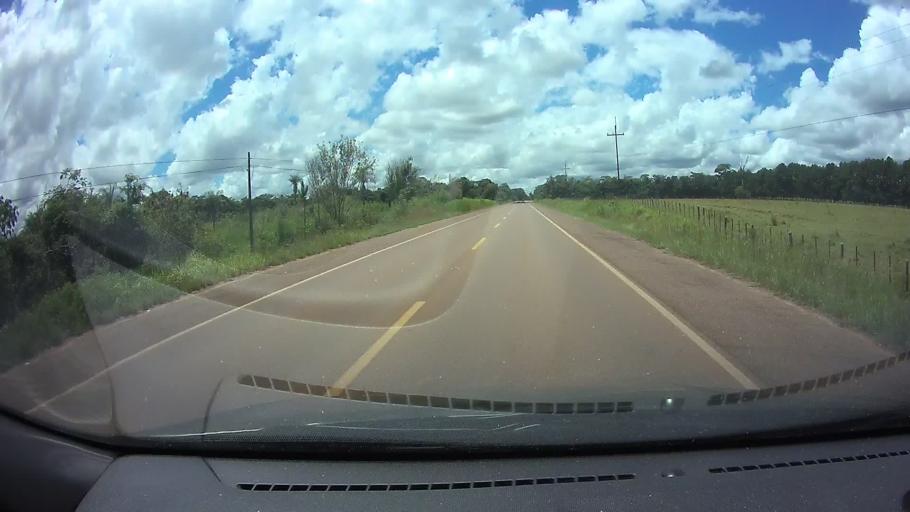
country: PY
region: Paraguari
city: La Colmena
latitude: -25.8907
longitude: -56.8074
